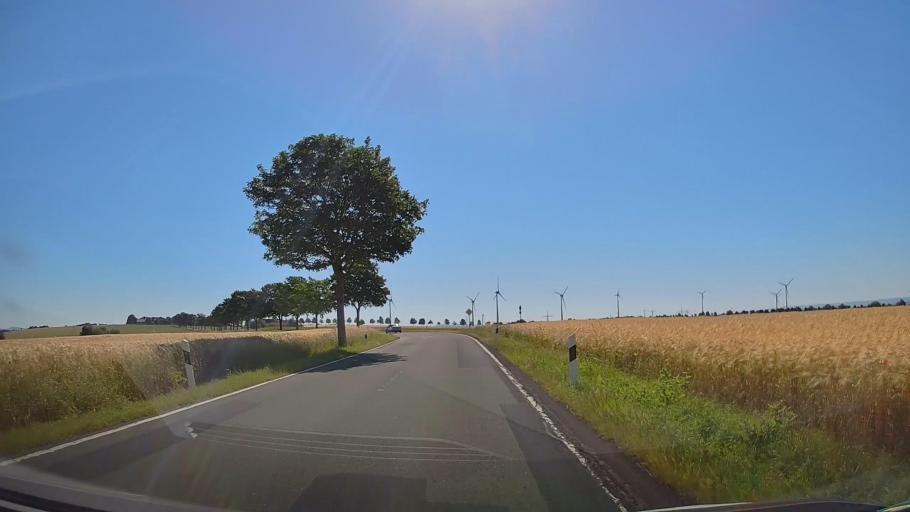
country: DE
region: Lower Saxony
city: Vahlbruch
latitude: 51.9553
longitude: 9.3089
